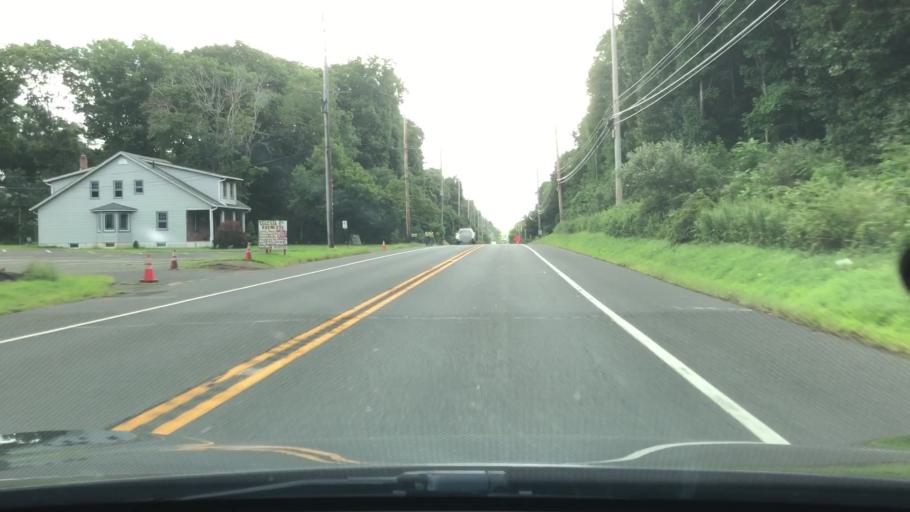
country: US
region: New Jersey
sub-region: Monmouth County
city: West Freehold
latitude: 40.2570
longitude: -74.3126
